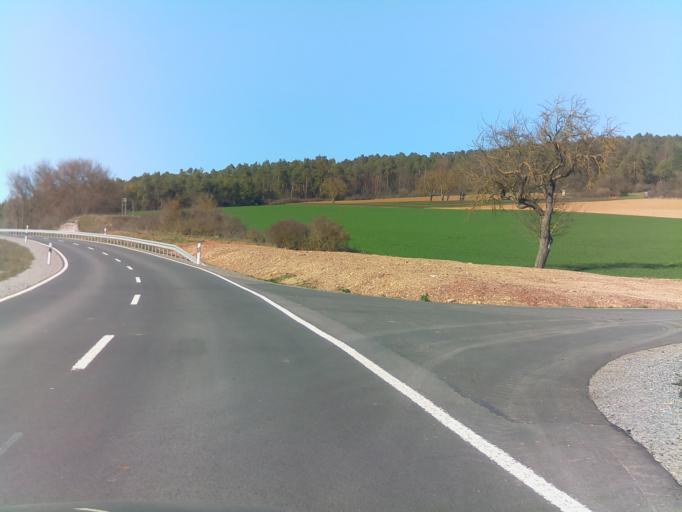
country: DE
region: Bavaria
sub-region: Regierungsbezirk Unterfranken
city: Stockheim
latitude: 50.4643
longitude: 10.2640
